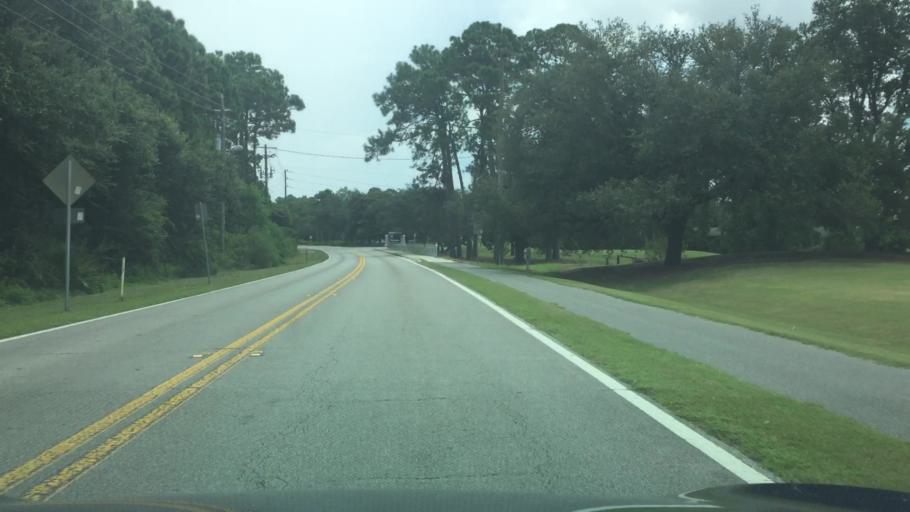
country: US
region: Florida
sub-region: Bay County
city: Upper Grand Lagoon
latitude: 30.1519
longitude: -85.7250
